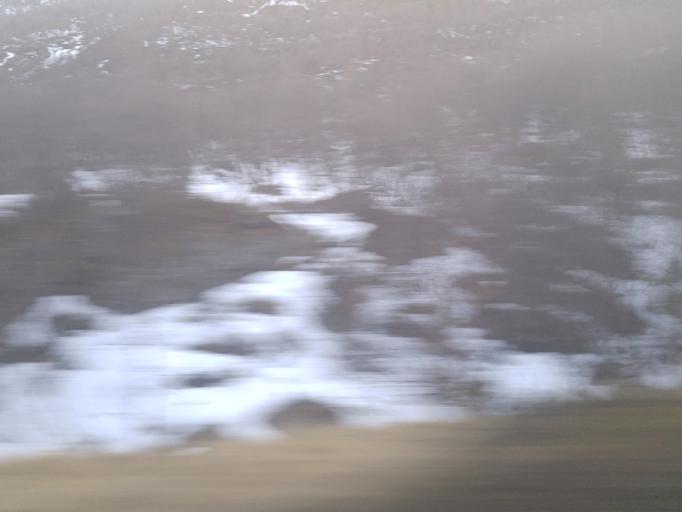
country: NO
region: Sor-Trondelag
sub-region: Oppdal
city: Oppdal
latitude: 62.3190
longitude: 9.6175
